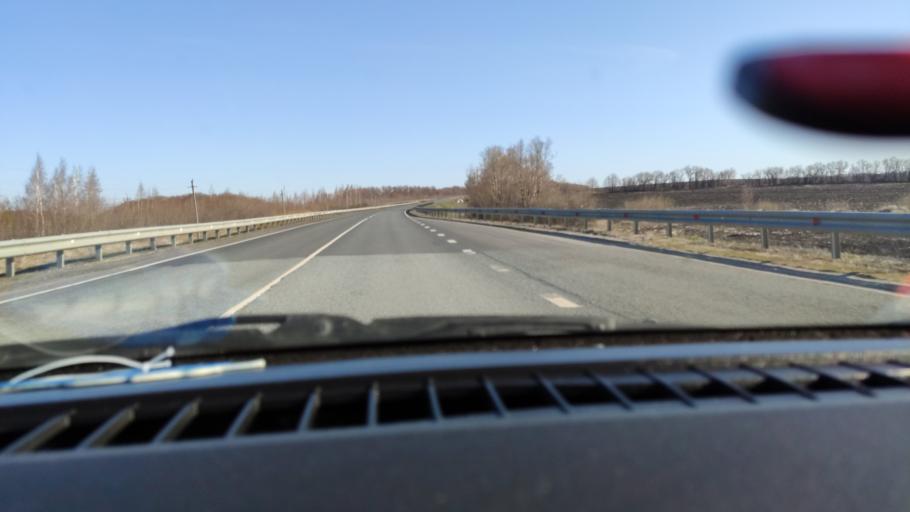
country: RU
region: Samara
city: Syzran'
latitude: 52.9730
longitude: 48.3087
